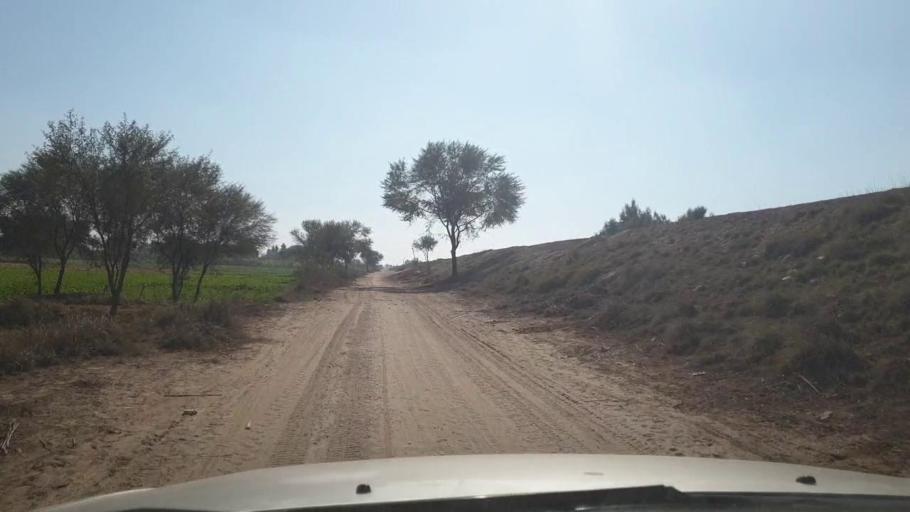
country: PK
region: Sindh
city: Ghotki
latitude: 28.0285
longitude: 69.2105
